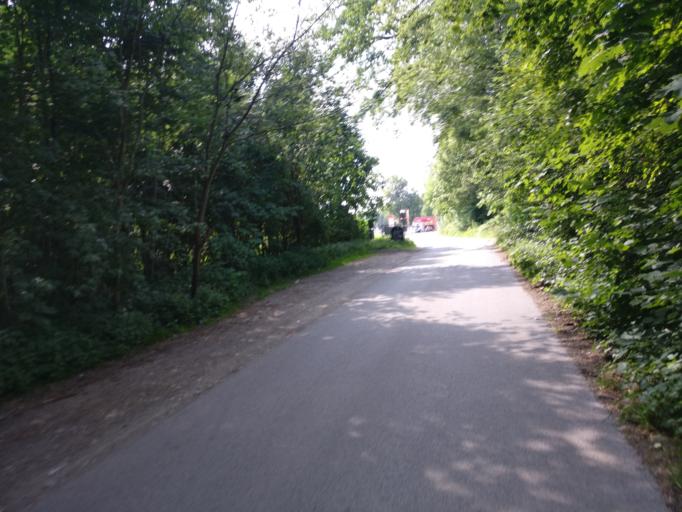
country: AT
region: Salzburg
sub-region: Politischer Bezirk Salzburg-Umgebung
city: Anif
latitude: 47.7368
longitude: 13.0712
